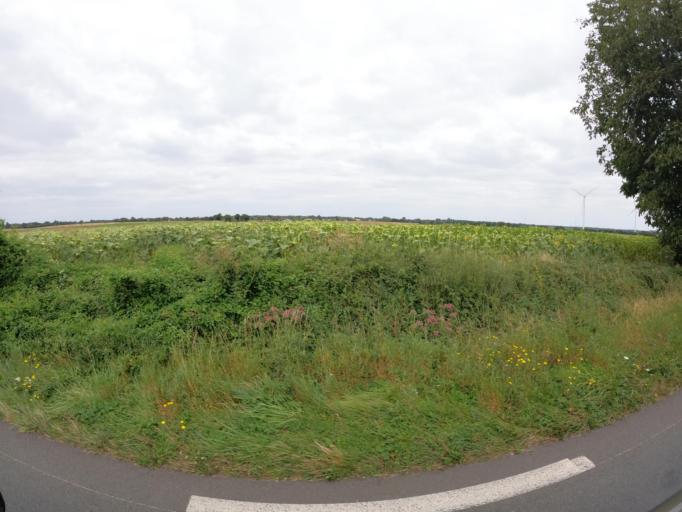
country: FR
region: Poitou-Charentes
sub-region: Departement des Deux-Sevres
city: Sauze-Vaussais
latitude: 46.1457
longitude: 0.0774
